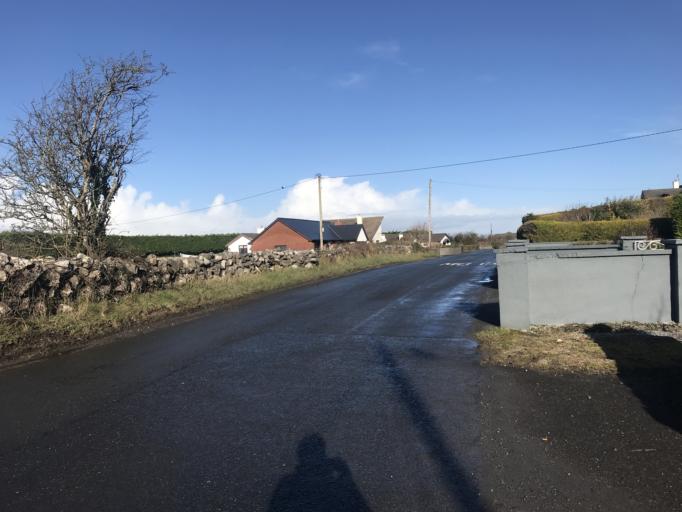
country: IE
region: Connaught
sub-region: County Galway
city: Gaillimh
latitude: 53.3027
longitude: -9.0199
